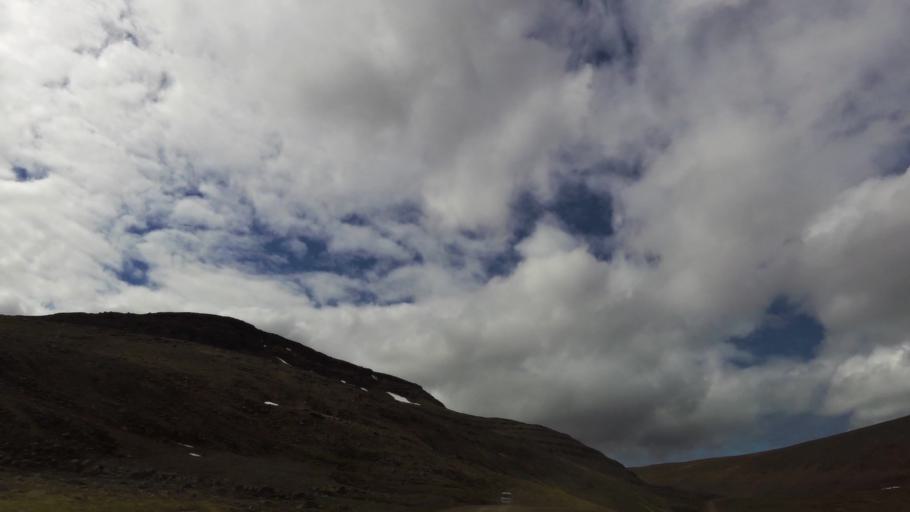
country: IS
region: Westfjords
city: Isafjoerdur
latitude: 66.1654
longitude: -23.3374
